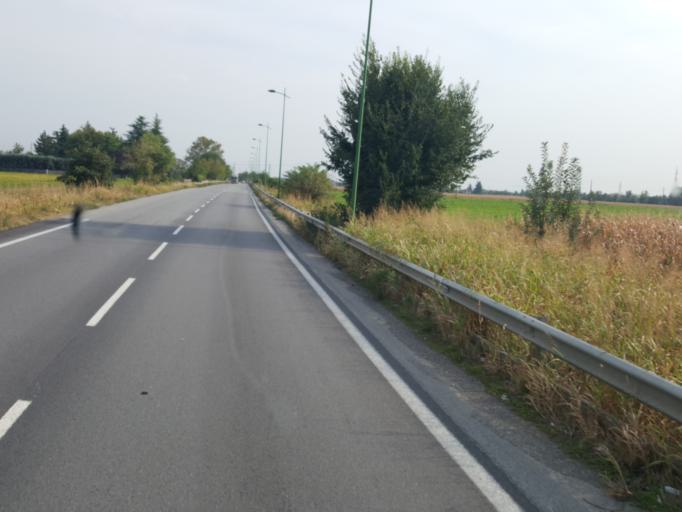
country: IT
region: Lombardy
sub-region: Provincia di Bergamo
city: Grassobbio
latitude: 45.6484
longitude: 9.7440
